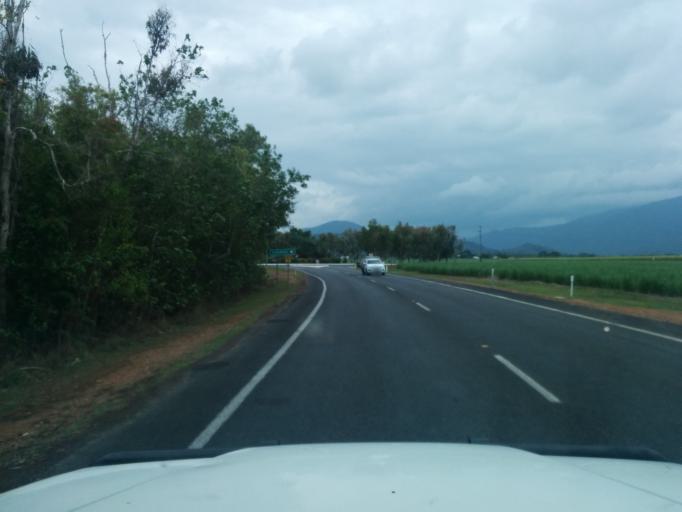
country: AU
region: Queensland
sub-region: Cairns
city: Redlynch
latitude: -16.8495
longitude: 145.7336
